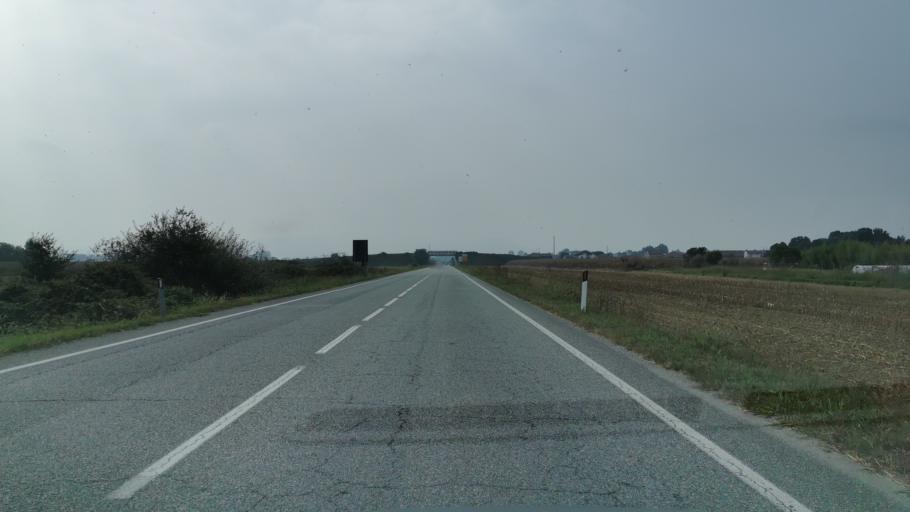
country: IT
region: Piedmont
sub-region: Provincia di Torino
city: Montanaro
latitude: 45.2377
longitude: 7.8647
